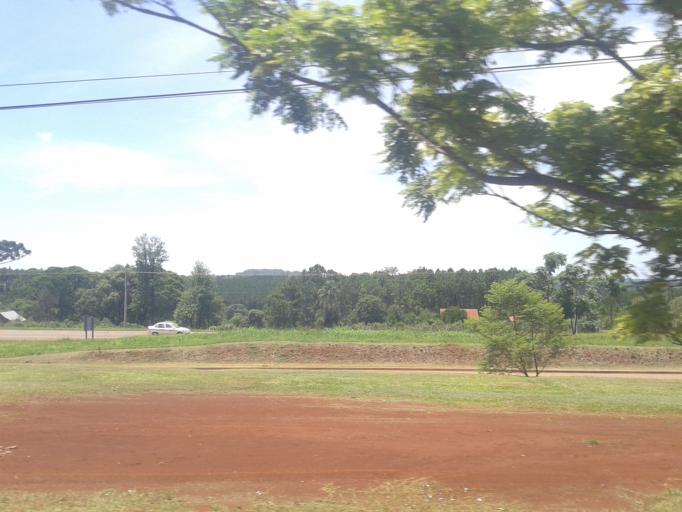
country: AR
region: Misiones
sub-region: Departamento de Leandro N. Alem
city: Leandro N. Alem
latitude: -27.6219
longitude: -55.3356
